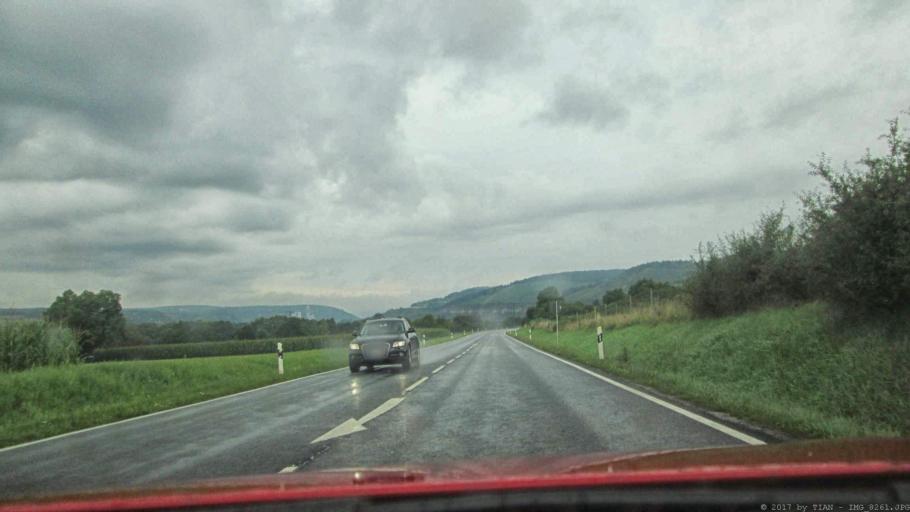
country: DE
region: Bavaria
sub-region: Regierungsbezirk Unterfranken
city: Himmelstadt
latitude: 49.9264
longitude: 9.8119
